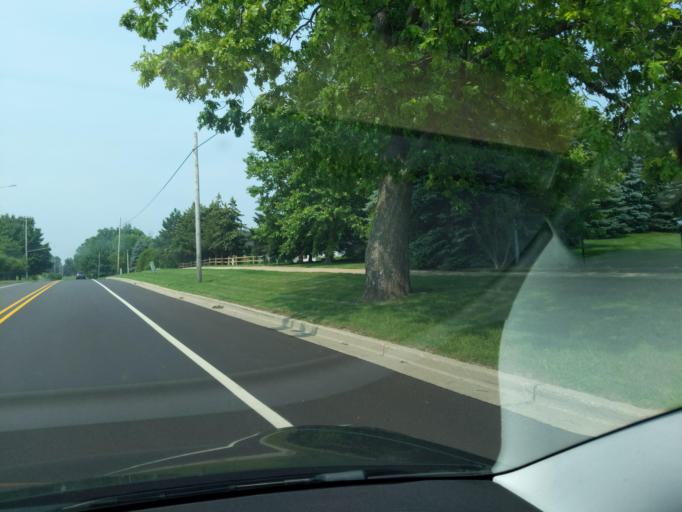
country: US
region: Michigan
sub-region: Clinton County
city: DeWitt
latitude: 42.8290
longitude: -84.5724
